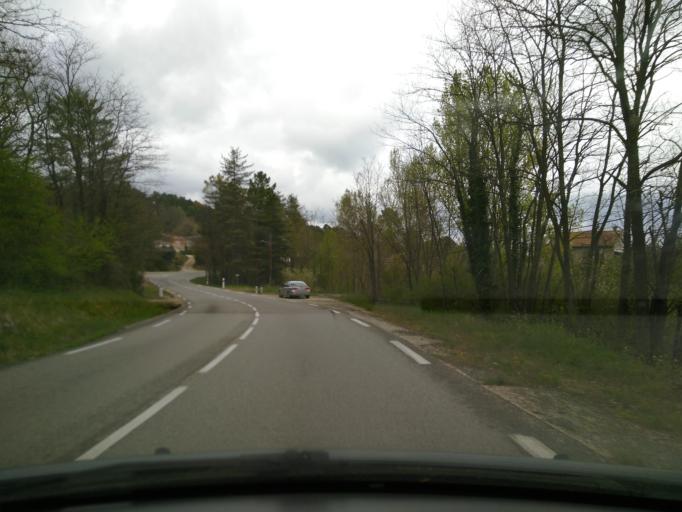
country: FR
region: Languedoc-Roussillon
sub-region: Departement du Gard
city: Barjac
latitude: 44.3762
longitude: 4.3712
